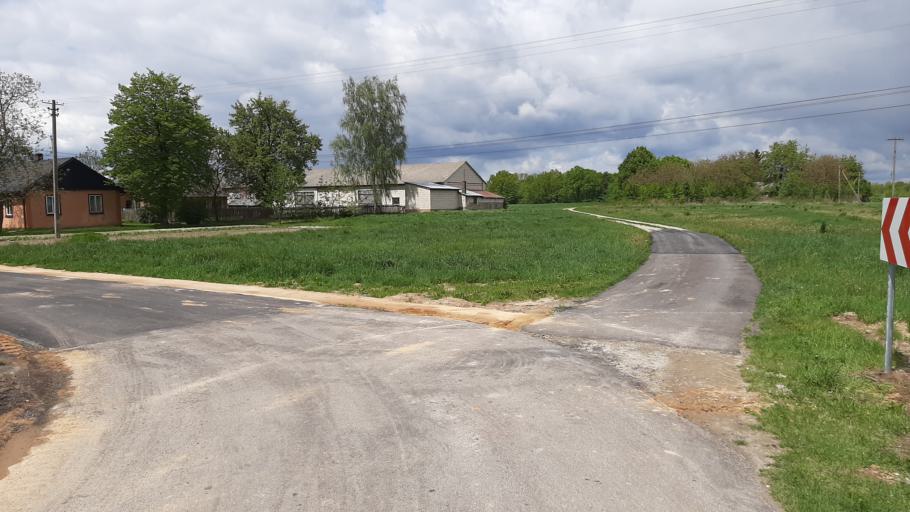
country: PL
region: Lublin Voivodeship
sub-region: Powiat lubelski
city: Jastkow
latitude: 51.3641
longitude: 22.4050
